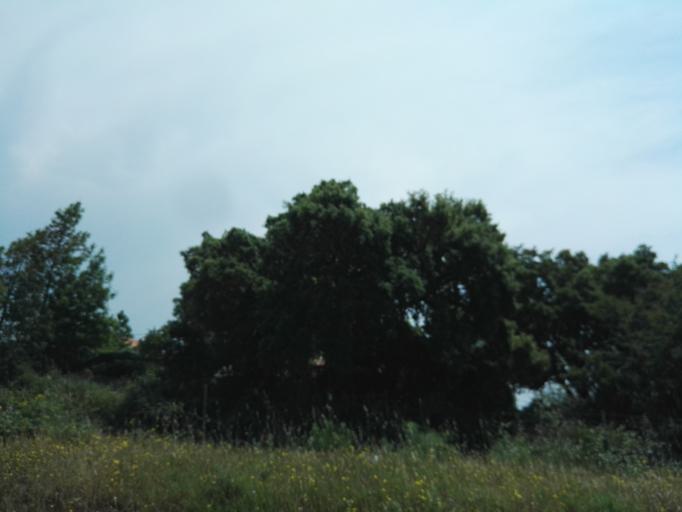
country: PT
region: Santarem
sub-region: Entroncamento
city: Entroncamento
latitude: 39.4763
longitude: -8.4590
